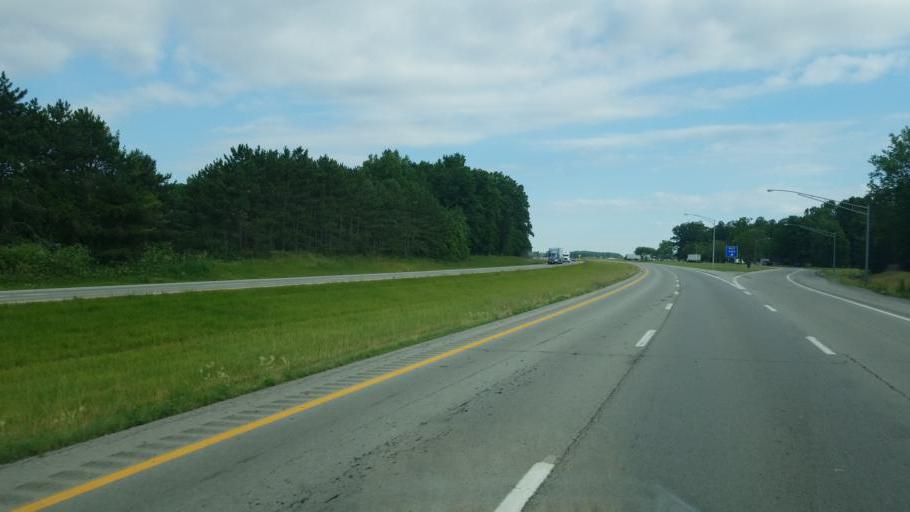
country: US
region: Ohio
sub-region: Wyandot County
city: Carey
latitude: 40.9187
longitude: -83.3550
